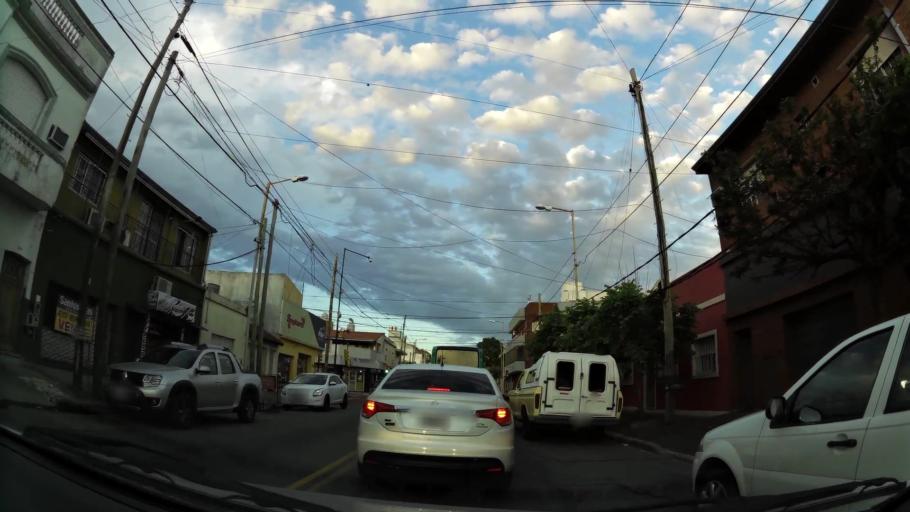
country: AR
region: Buenos Aires
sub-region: Partido de Avellaneda
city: Avellaneda
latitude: -34.6992
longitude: -58.3287
